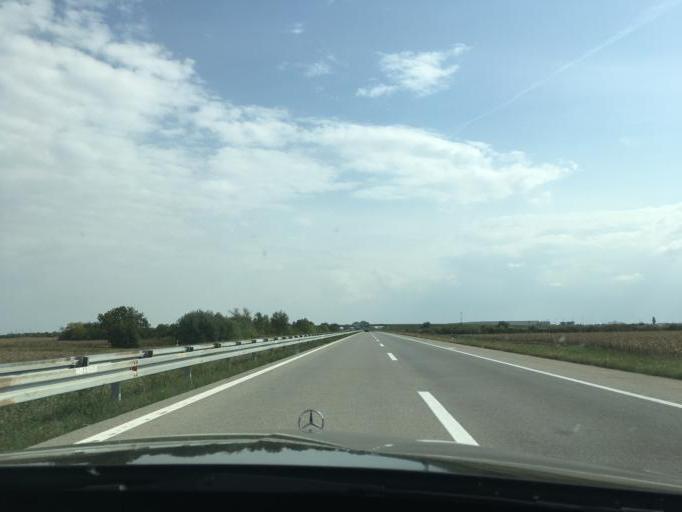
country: RS
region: Autonomna Pokrajina Vojvodina
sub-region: Sremski Okrug
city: Sremska Mitrovica
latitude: 45.0064
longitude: 19.6031
